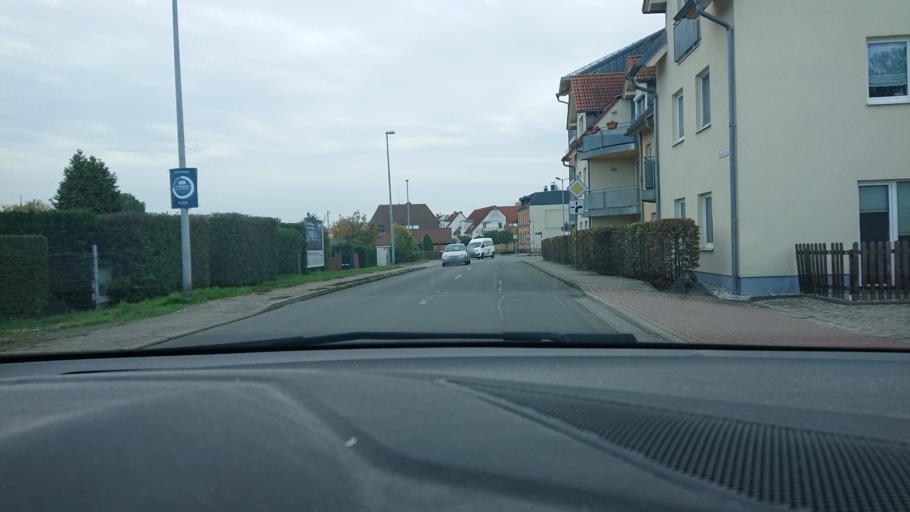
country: DE
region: Saxony
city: Delitzsch
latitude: 51.5217
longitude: 12.3215
